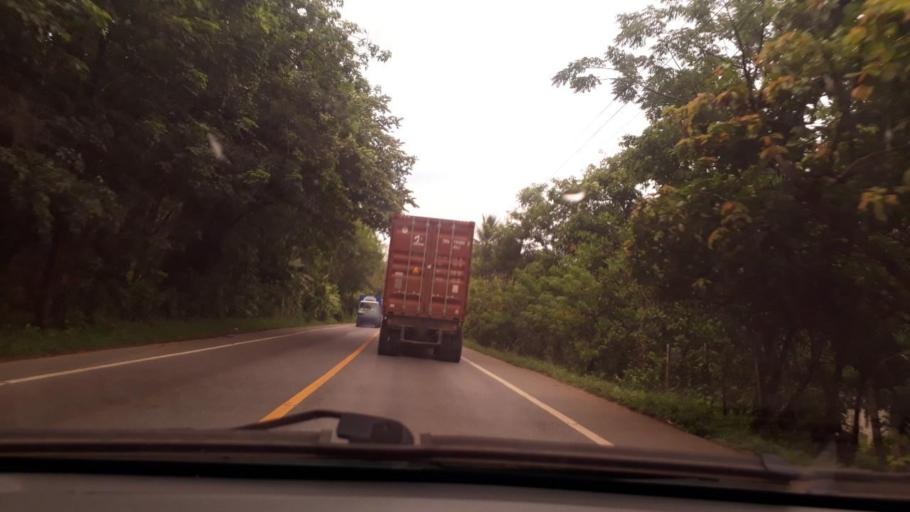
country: GT
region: Izabal
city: Morales
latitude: 15.5559
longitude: -88.6769
